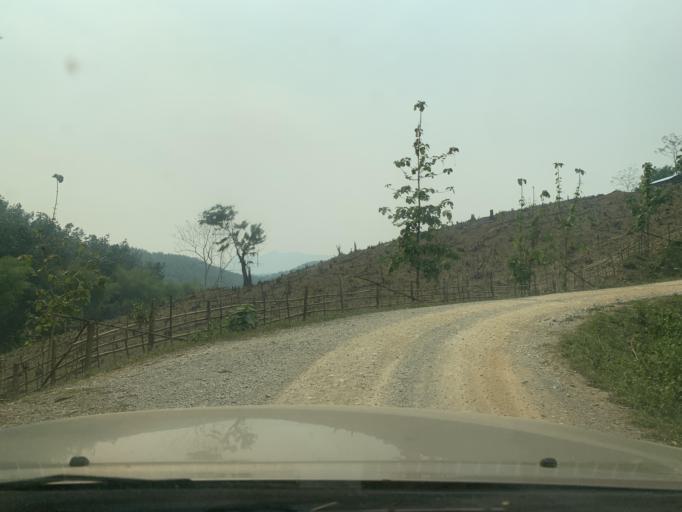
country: LA
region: Louangphabang
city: Louangphabang
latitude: 19.8901
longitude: 102.2506
